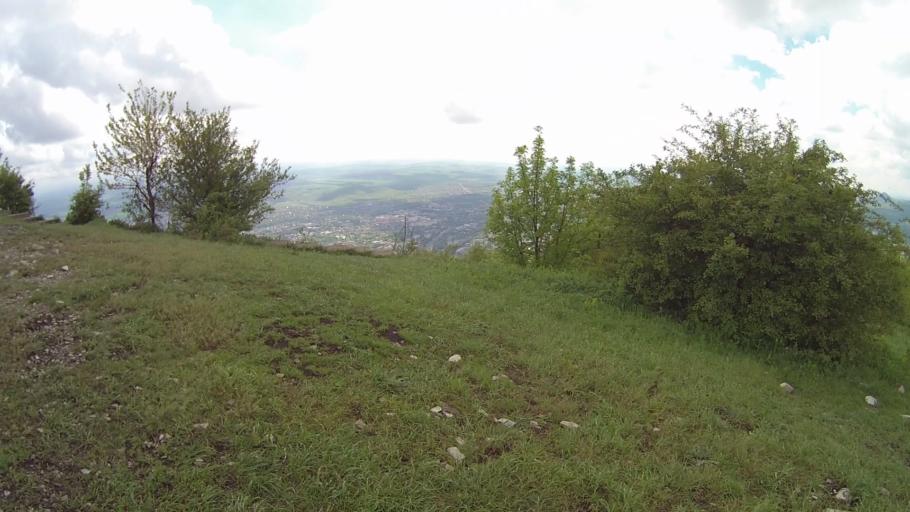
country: RU
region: Stavropol'skiy
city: Goryachevodskiy
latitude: 44.0507
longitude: 43.0875
